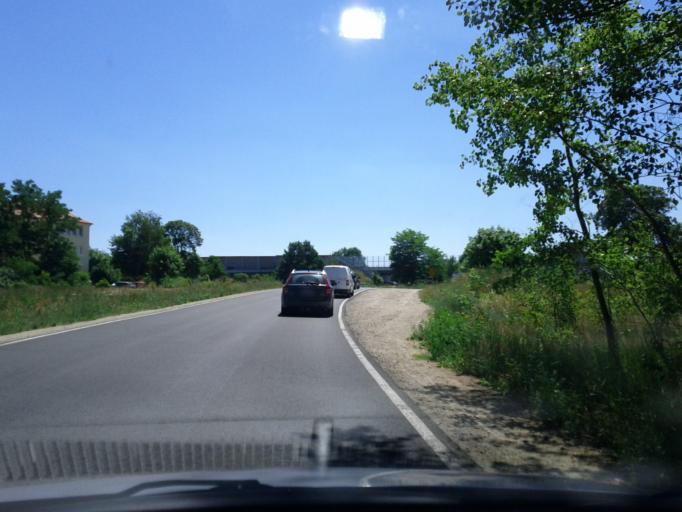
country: DE
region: Brandenburg
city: Langewahl
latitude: 52.3370
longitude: 14.0836
